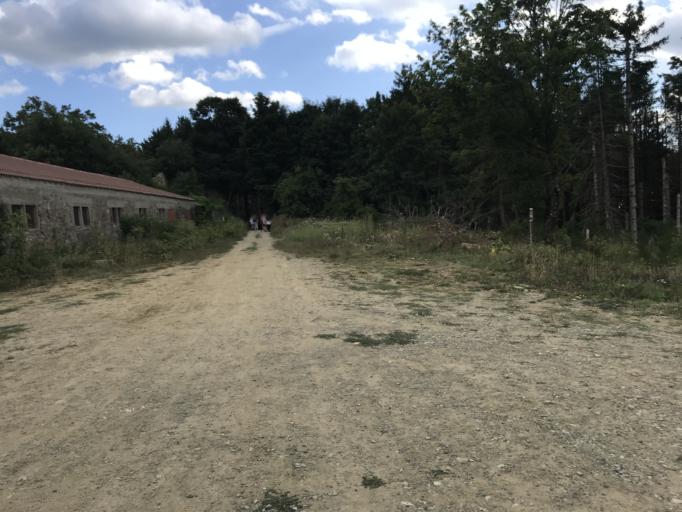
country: IT
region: Emilia-Romagna
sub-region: Provincia di Bologna
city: San Benedetto Val di Sambro
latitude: 44.1531
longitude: 11.2625
